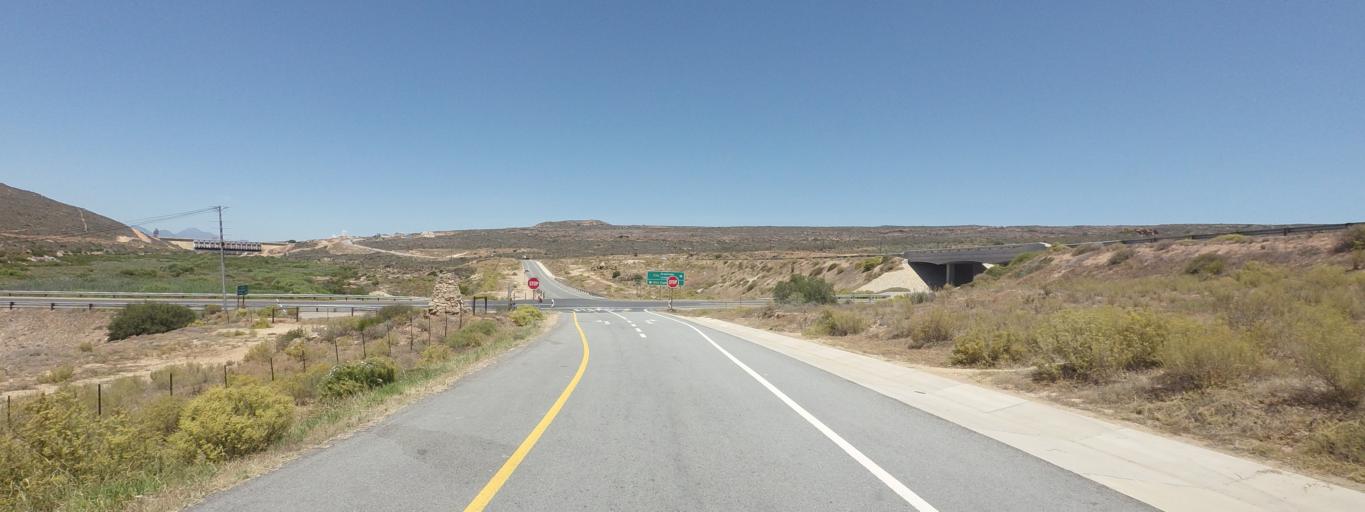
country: ZA
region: Western Cape
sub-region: West Coast District Municipality
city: Clanwilliam
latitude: -32.1725
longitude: 18.8683
